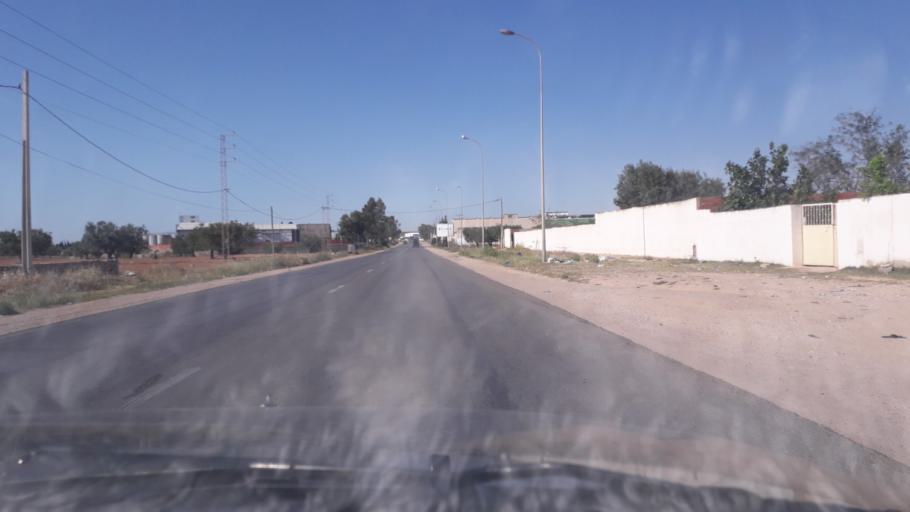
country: TN
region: Safaqis
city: Al Qarmadah
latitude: 34.8818
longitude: 10.7599
